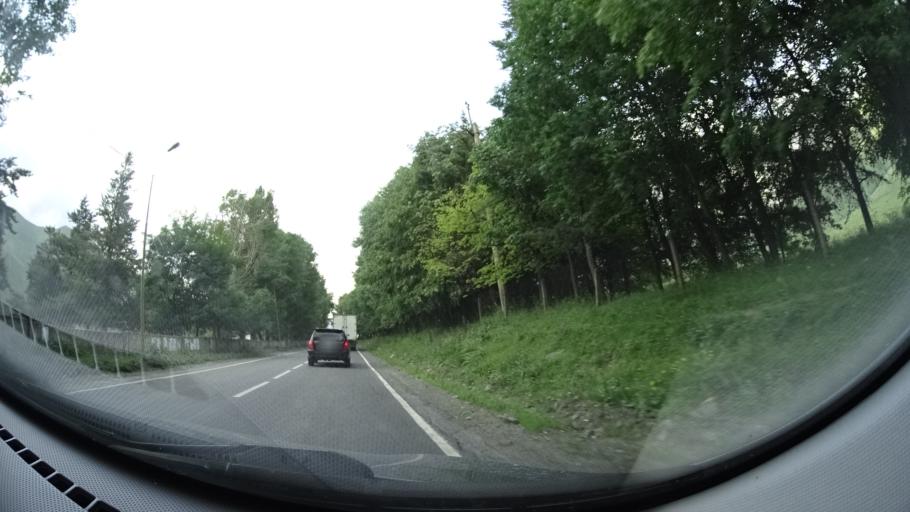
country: GE
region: Mtskheta-Mtianeti
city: Step'antsminda
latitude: 42.6484
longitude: 44.6415
